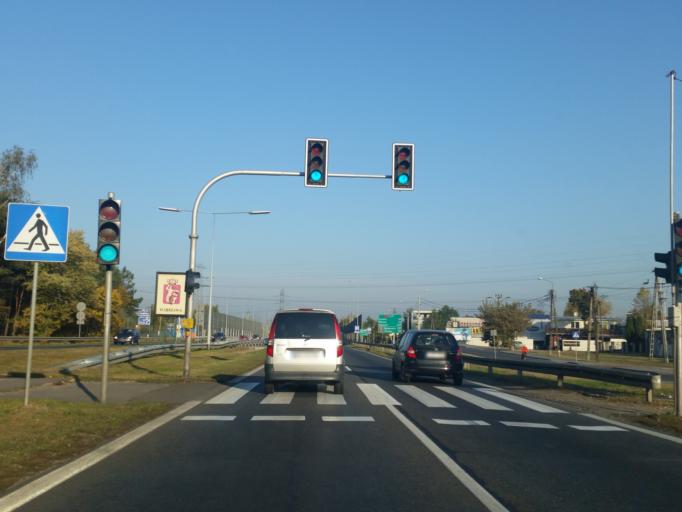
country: PL
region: Masovian Voivodeship
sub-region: Powiat warszawski zachodni
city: Lomianki
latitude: 52.3229
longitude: 20.9115
